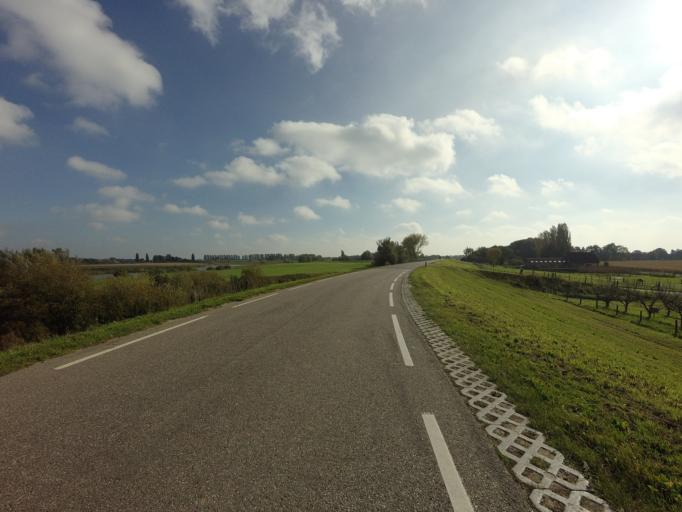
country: NL
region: Gelderland
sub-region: Gemeente Culemborg
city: Culemborg
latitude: 51.9626
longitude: 5.2653
